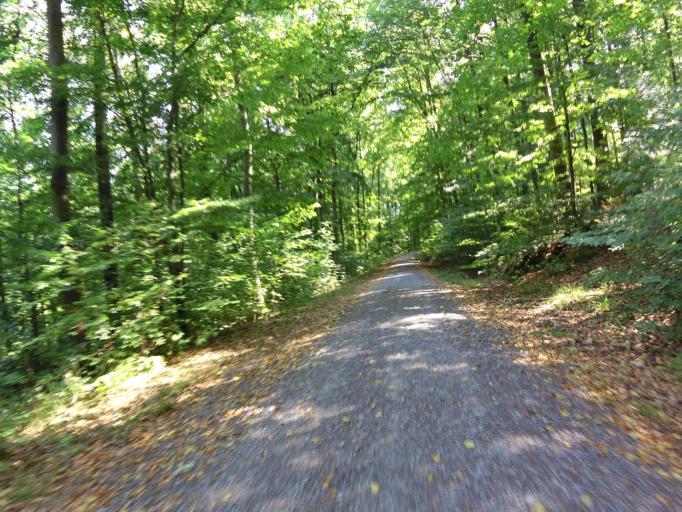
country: DE
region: Bavaria
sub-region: Regierungsbezirk Unterfranken
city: Wuerzburg
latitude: 49.7673
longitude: 9.8891
